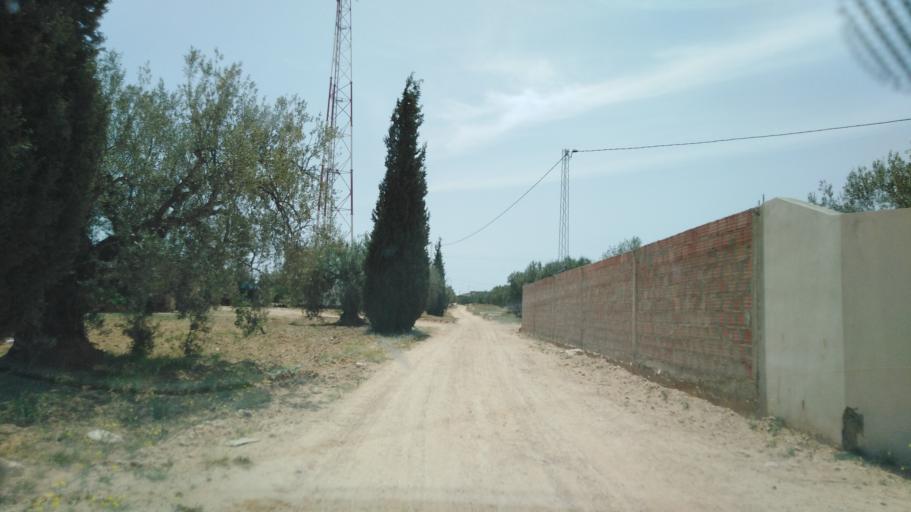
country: TN
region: Safaqis
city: Sfax
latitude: 34.7315
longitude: 10.5560
